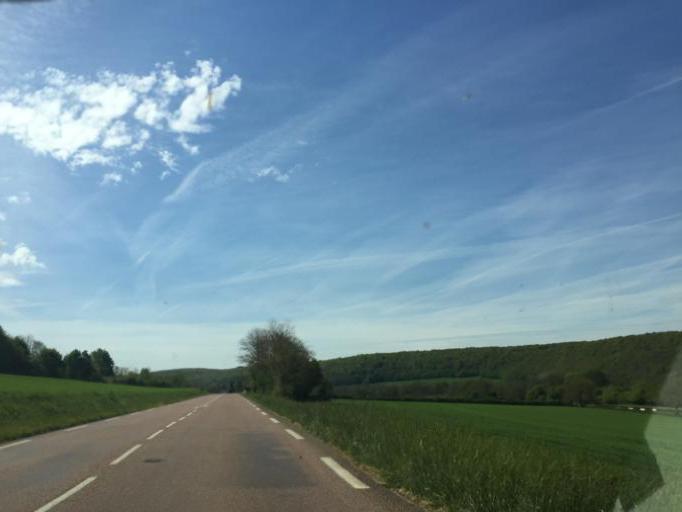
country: FR
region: Bourgogne
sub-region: Departement de la Nievre
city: Clamecy
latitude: 47.4389
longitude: 3.5579
